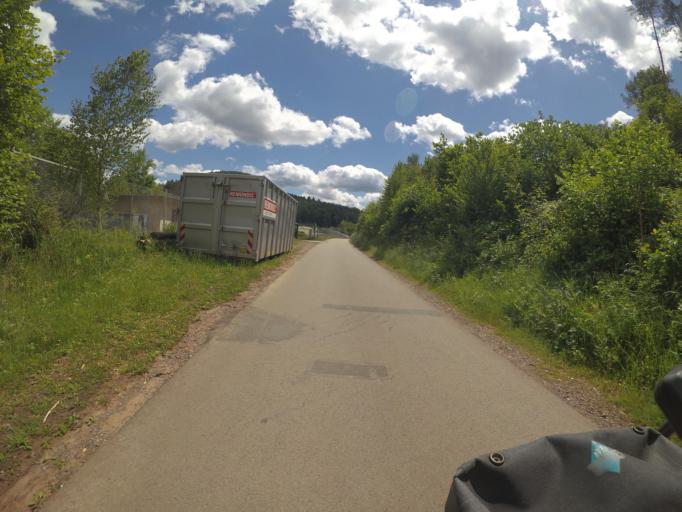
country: DE
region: Rheinland-Pfalz
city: Bruchweiler-Barenbach
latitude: 49.1368
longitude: 7.7981
